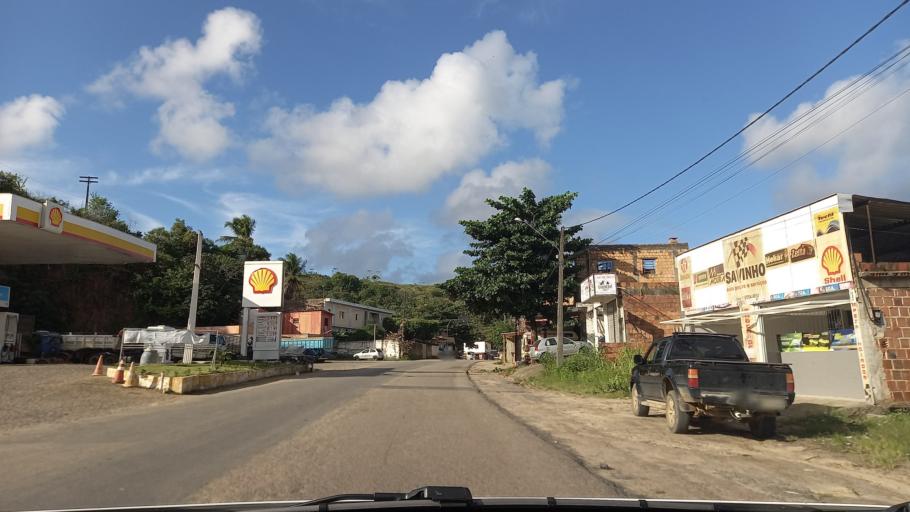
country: BR
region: Pernambuco
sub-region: Rio Formoso
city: Rio Formoso
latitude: -8.6580
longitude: -35.1553
